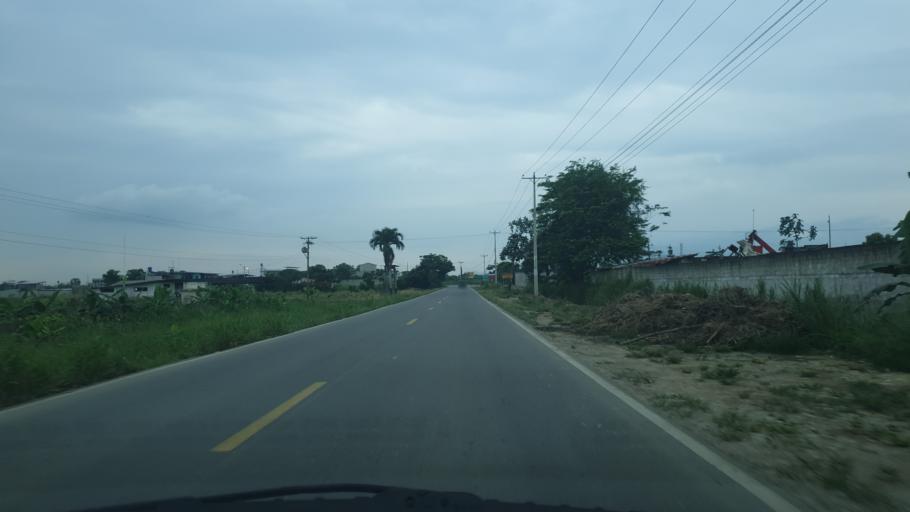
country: EC
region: El Oro
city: Pasaje
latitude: -3.3487
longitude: -79.8144
